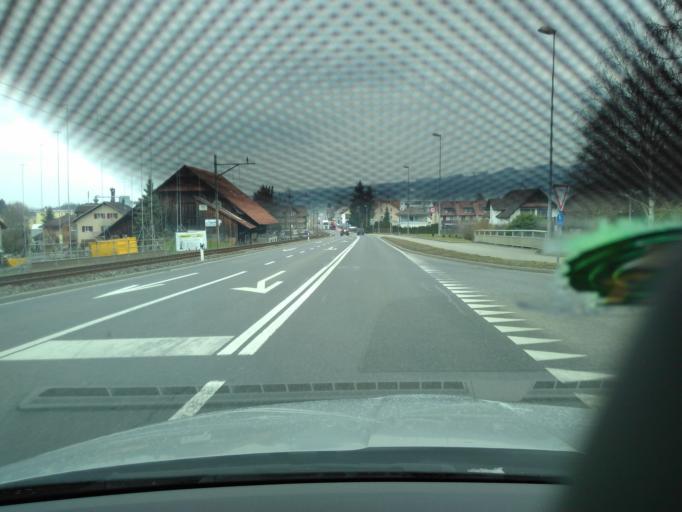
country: CH
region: Lucerne
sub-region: Hochdorf District
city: Hochdorf
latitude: 47.1823
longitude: 8.2808
